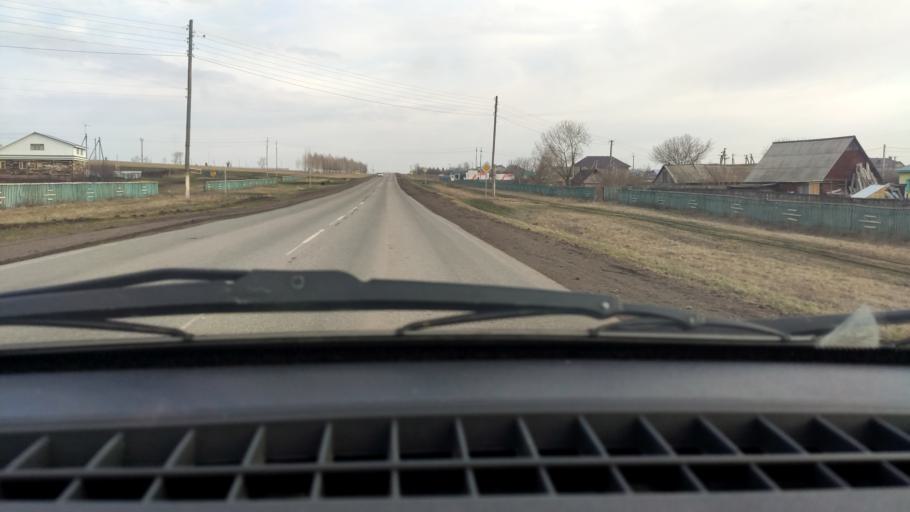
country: RU
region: Bashkortostan
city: Davlekanovo
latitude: 54.3697
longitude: 55.1953
